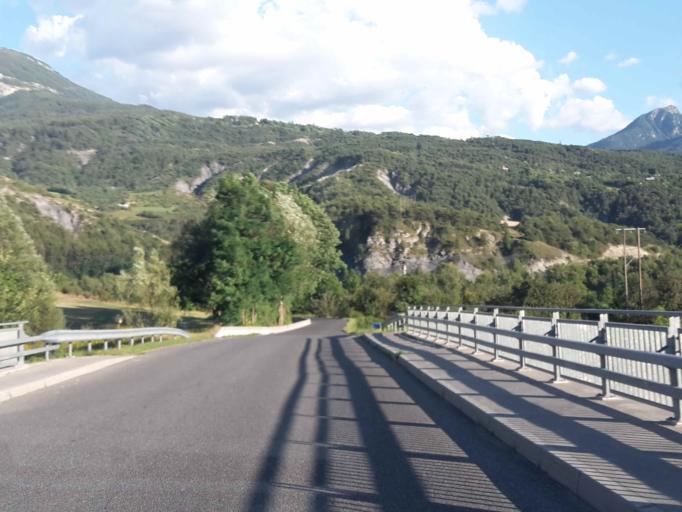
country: FR
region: Provence-Alpes-Cote d'Azur
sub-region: Departement des Hautes-Alpes
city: Embrun
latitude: 44.5634
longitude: 6.5071
